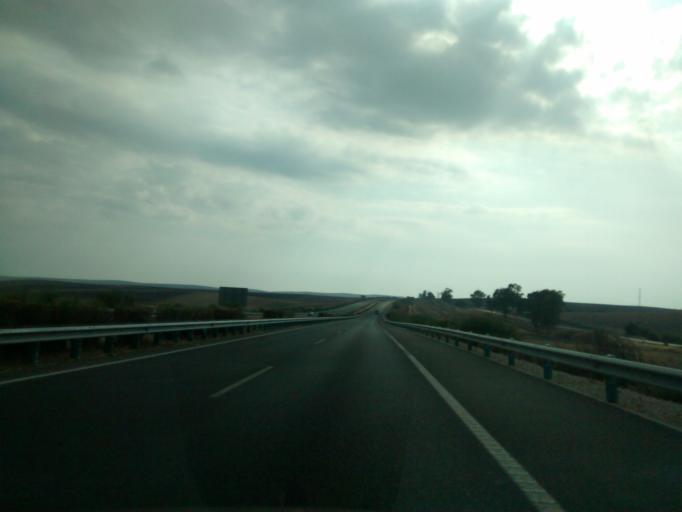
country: ES
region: Andalusia
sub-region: Provincia de Cadiz
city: Arcos de la Frontera
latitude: 36.7378
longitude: -5.8891
